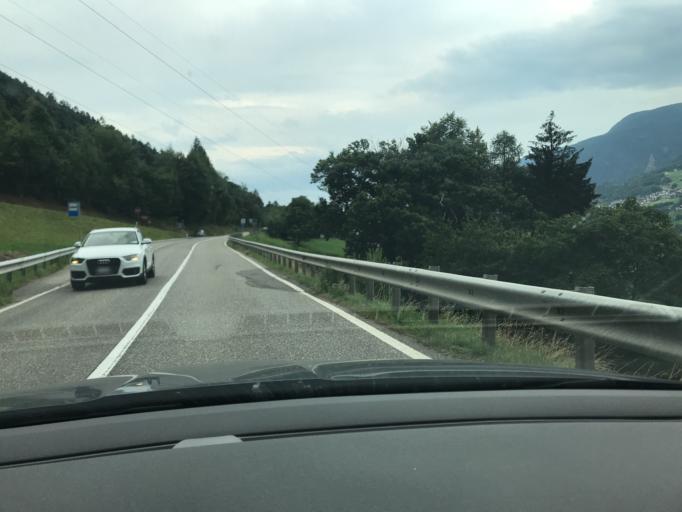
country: IT
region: Trentino-Alto Adige
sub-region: Bolzano
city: Villandro
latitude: 46.6179
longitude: 11.5479
